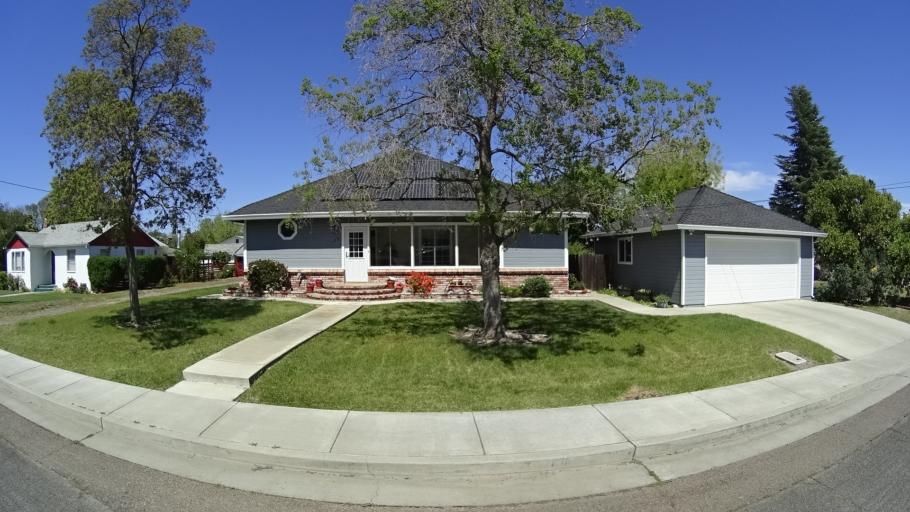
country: US
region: California
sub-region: Glenn County
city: Orland
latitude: 39.7439
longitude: -122.1836
